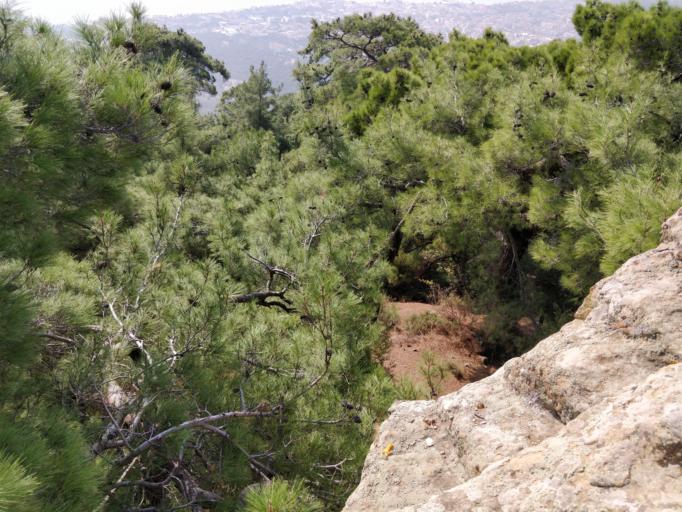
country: TR
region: Canakkale
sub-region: Merkez
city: Kucukkuyu
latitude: 39.5604
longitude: 26.6179
